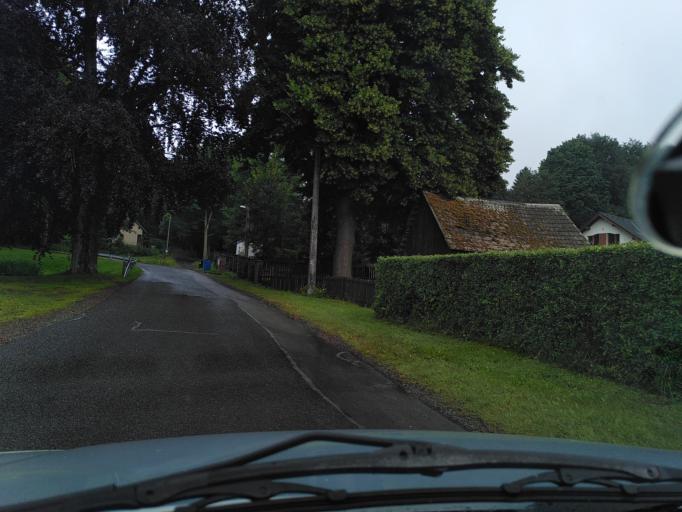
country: CZ
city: Novy Bor
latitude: 50.7857
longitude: 14.5272
